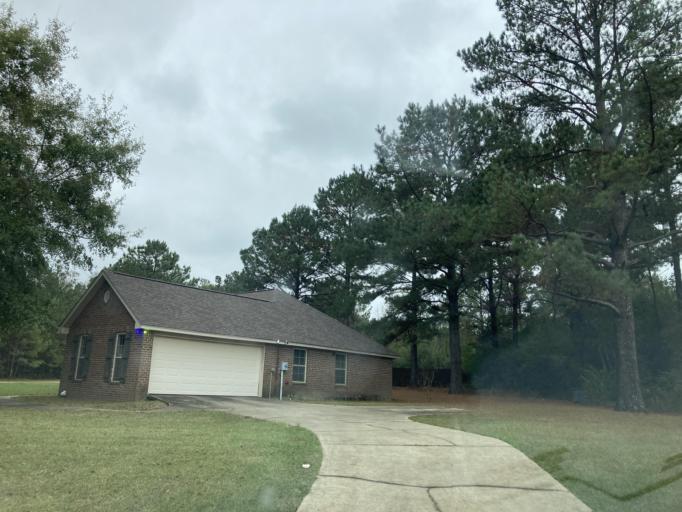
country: US
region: Mississippi
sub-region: Lamar County
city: West Hattiesburg
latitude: 31.2657
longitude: -89.4959
